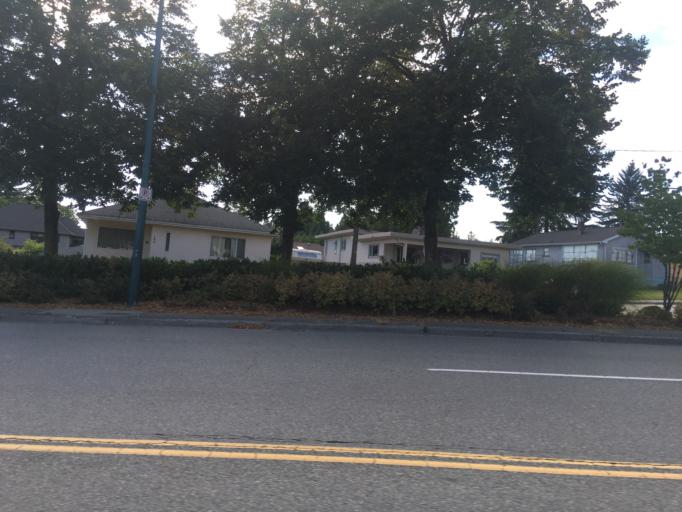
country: CA
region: British Columbia
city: Port Moody
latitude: 49.2459
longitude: -122.8727
